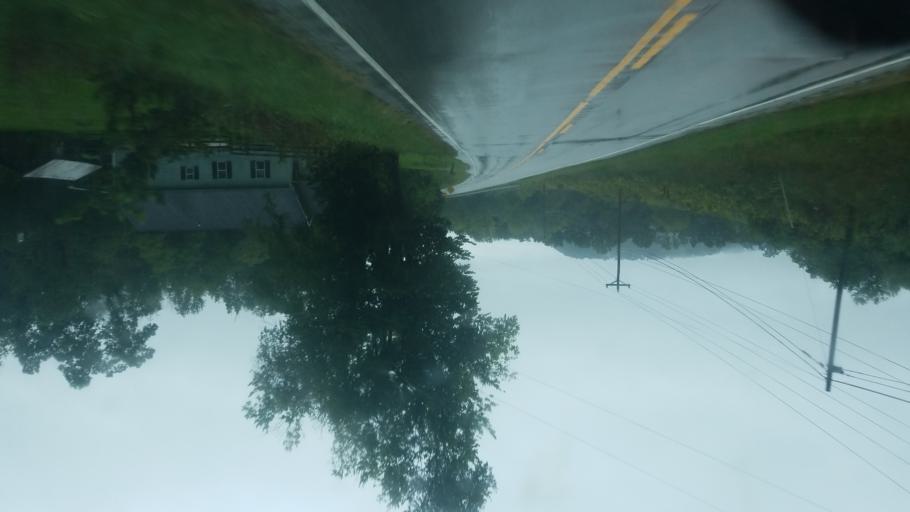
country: US
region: Kentucky
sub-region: Fleming County
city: Flemingsburg
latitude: 38.3520
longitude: -83.6082
